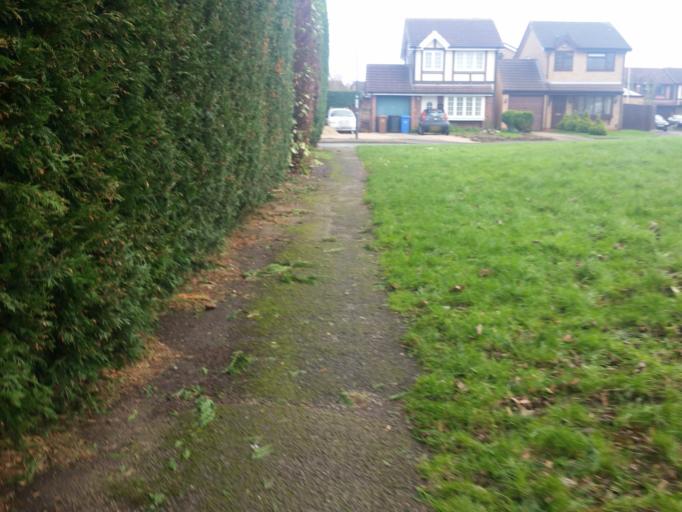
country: GB
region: England
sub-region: Derbyshire
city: Borrowash
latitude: 52.8934
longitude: -1.4141
